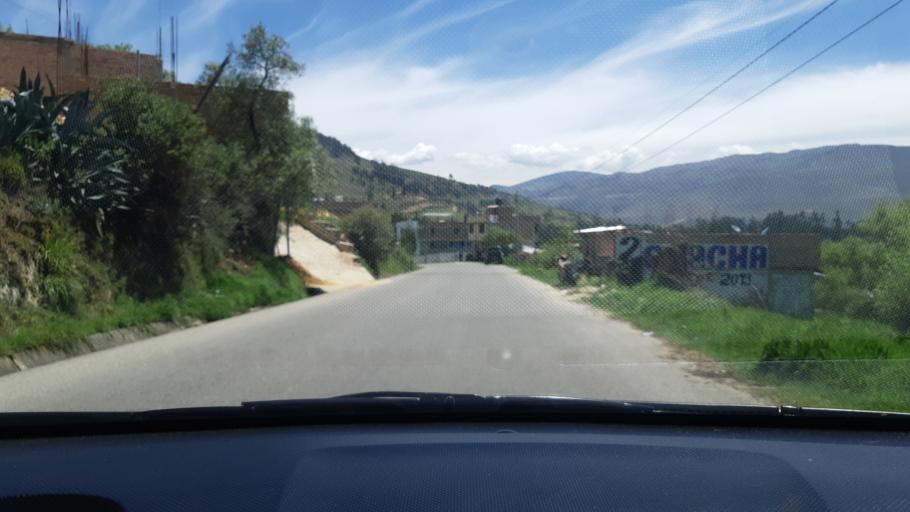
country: PE
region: Cajamarca
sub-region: Provincia de Cajamarca
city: Llacanora
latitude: -7.1783
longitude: -78.4567
